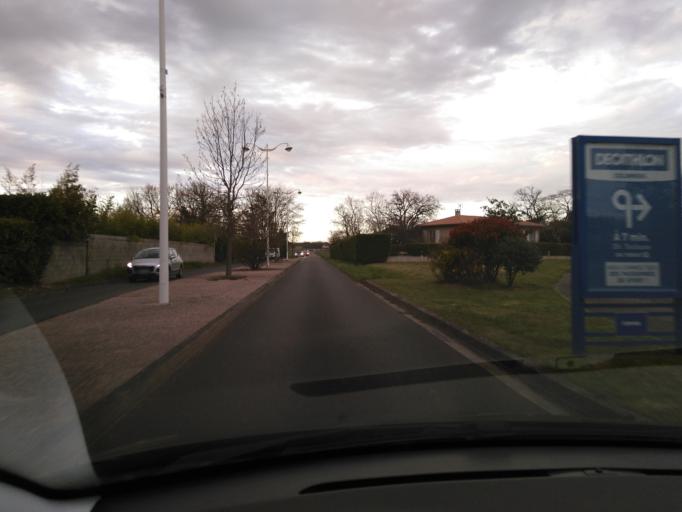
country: FR
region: Midi-Pyrenees
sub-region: Departement de la Haute-Garonne
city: La Salvetat-Saint-Gilles
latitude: 43.5803
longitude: 1.2676
